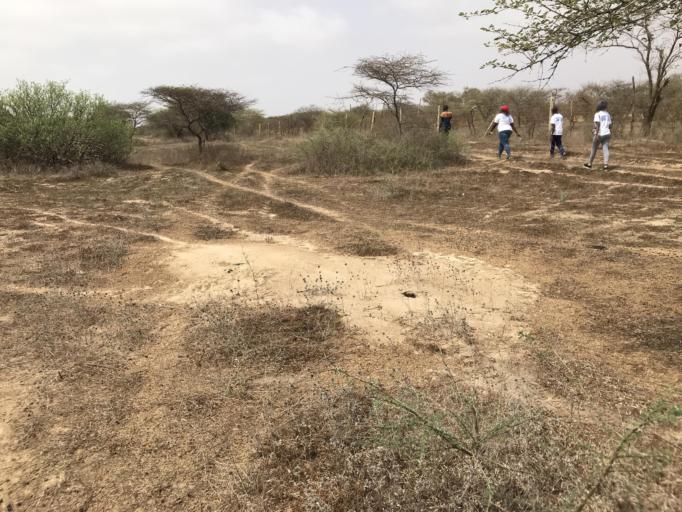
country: SN
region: Saint-Louis
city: Saint-Louis
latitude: 15.9133
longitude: -16.4551
